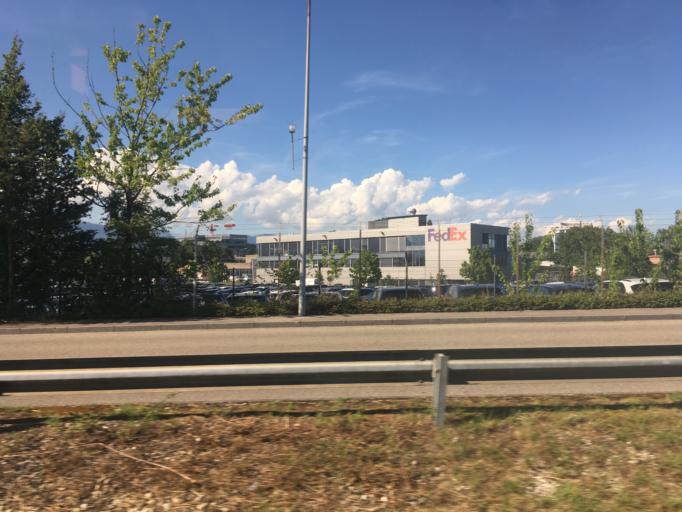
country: CH
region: Geneva
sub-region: Geneva
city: Vernier
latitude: 46.2226
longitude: 6.0803
